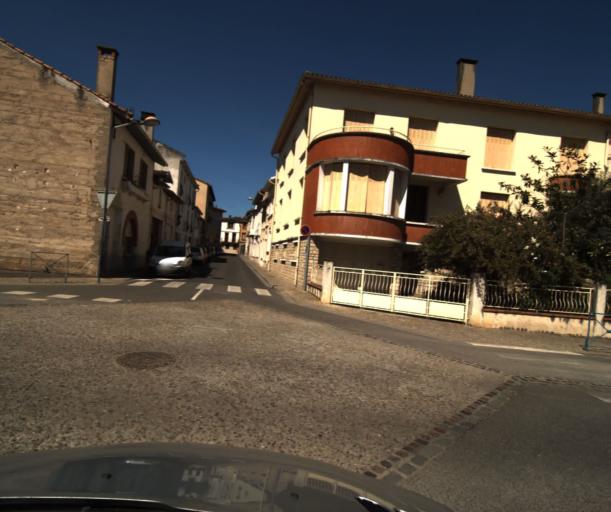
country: FR
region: Midi-Pyrenees
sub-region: Departement du Tarn-et-Garonne
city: Moissac
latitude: 44.1038
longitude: 1.0892
